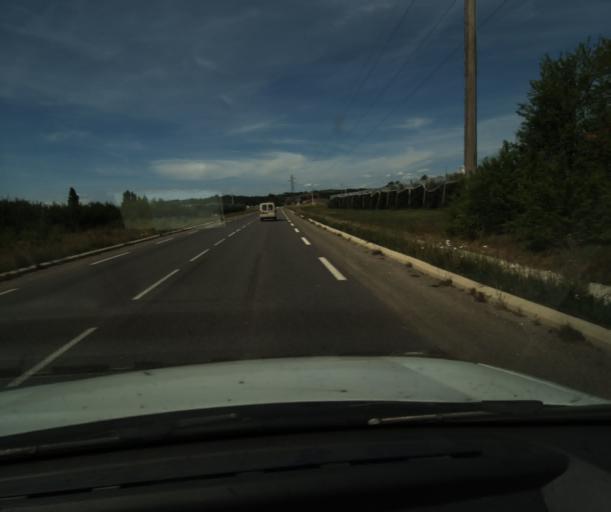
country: FR
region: Midi-Pyrenees
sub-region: Departement du Tarn-et-Garonne
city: Moissac
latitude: 44.1017
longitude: 1.1130
